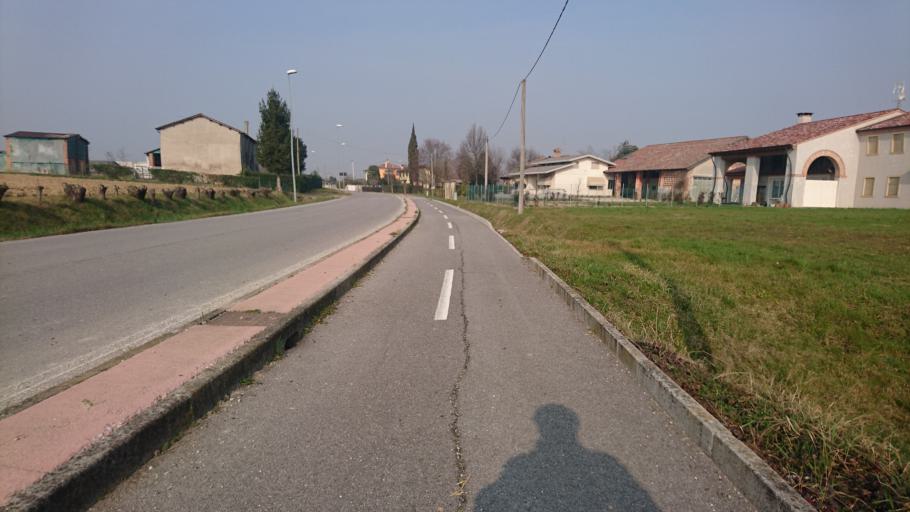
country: IT
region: Veneto
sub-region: Provincia di Padova
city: Veggiano
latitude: 45.4537
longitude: 11.7040
